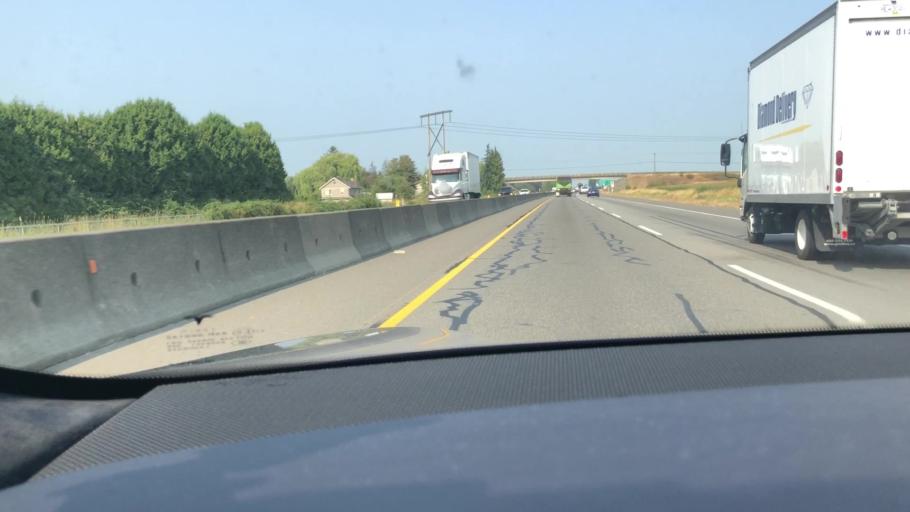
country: CA
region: British Columbia
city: Richmond
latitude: 49.1767
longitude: -123.0422
